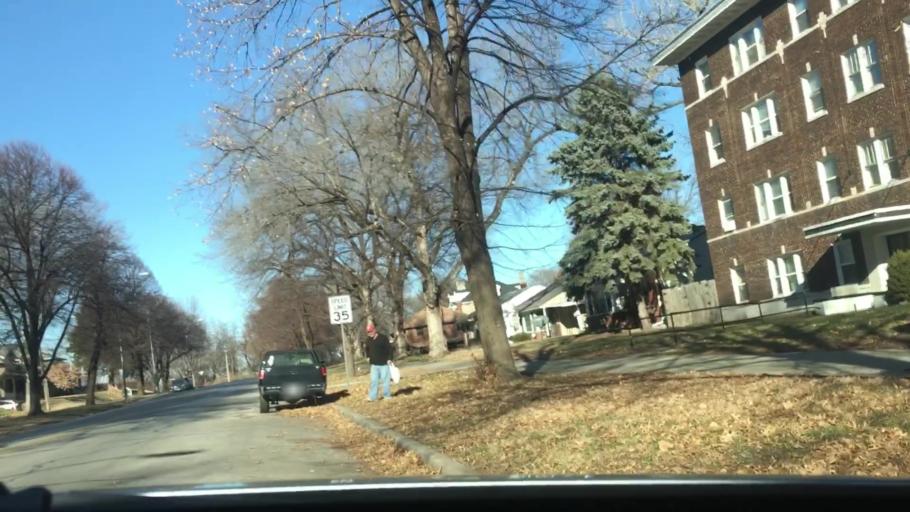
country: US
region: Missouri
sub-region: Clay County
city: North Kansas City
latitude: 39.1153
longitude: -94.5361
